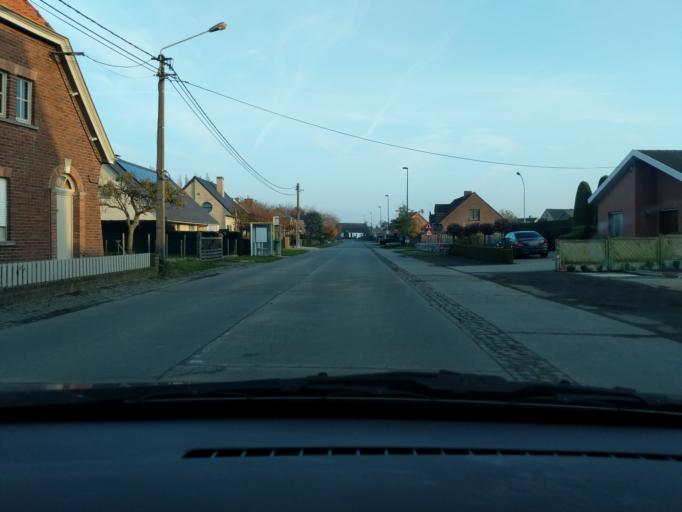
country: BE
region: Flanders
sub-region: Provincie Oost-Vlaanderen
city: Aalter
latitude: 51.0460
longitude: 3.4717
